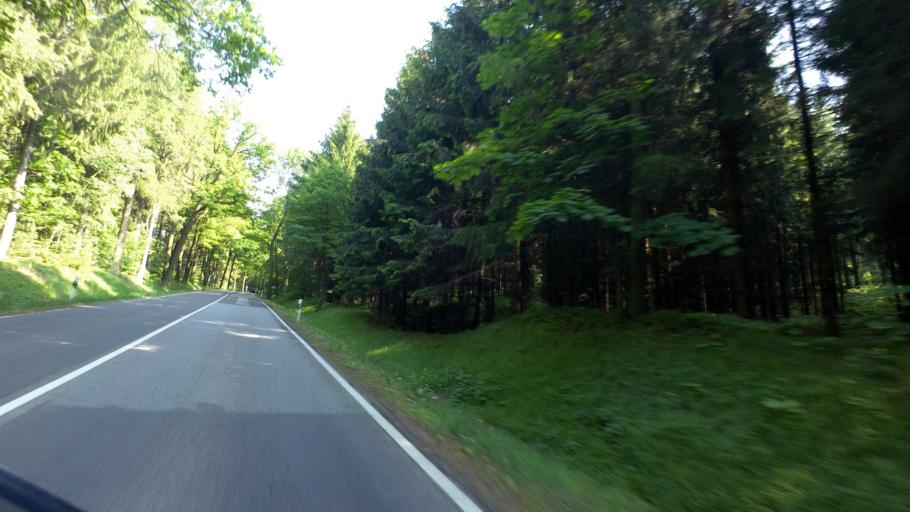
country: DE
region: Saxony
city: Oppach
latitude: 51.0764
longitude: 14.4872
